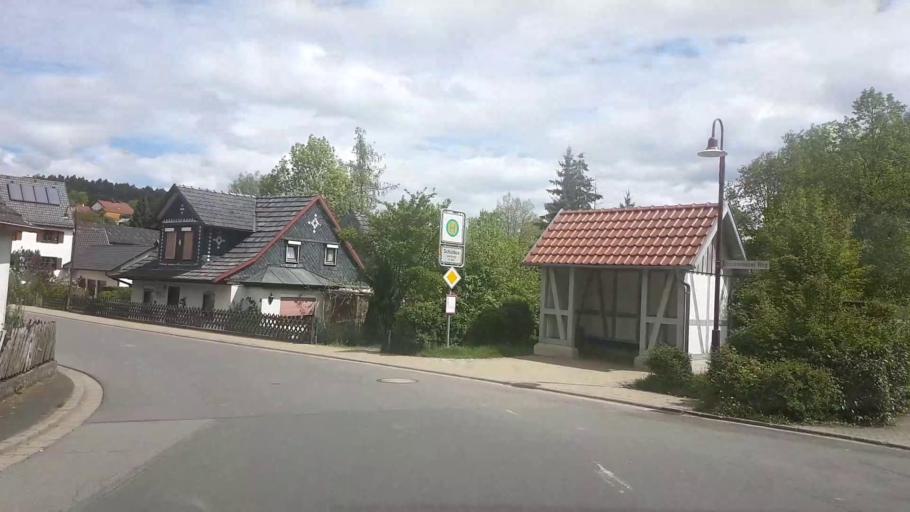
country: DE
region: Bavaria
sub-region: Upper Franconia
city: Untersiemau
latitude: 50.1984
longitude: 10.9917
